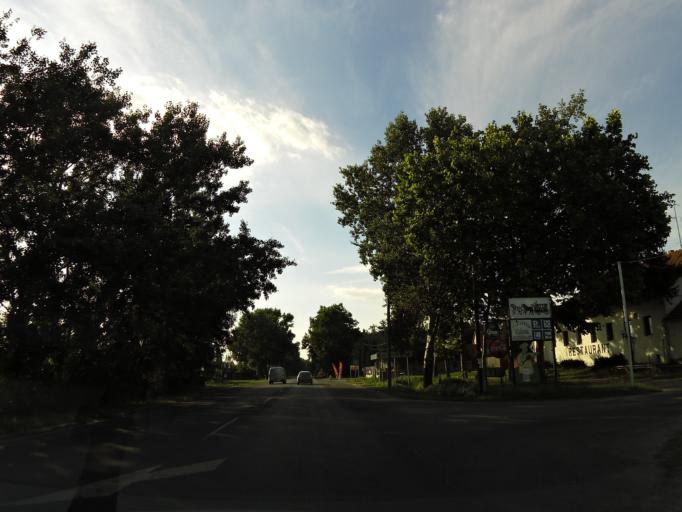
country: HU
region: Csongrad
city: Szatymaz
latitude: 46.3499
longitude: 20.0592
